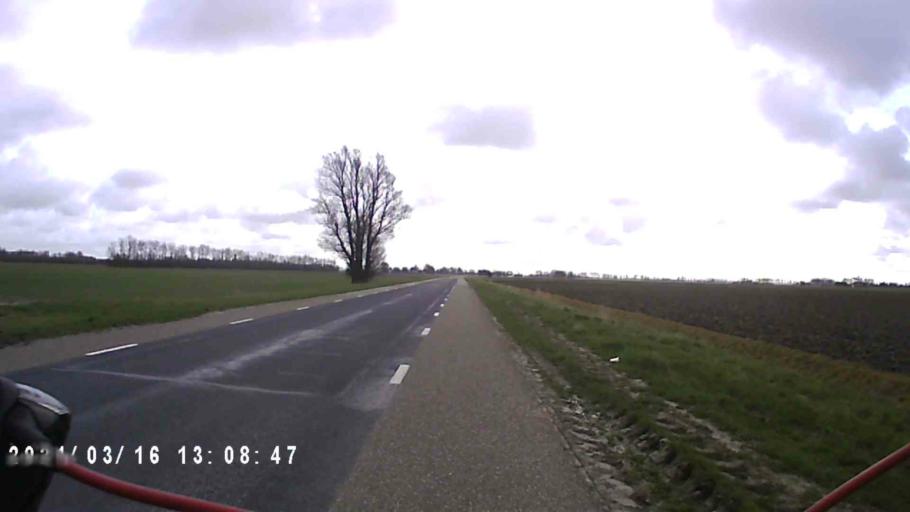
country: NL
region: Friesland
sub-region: Menameradiel
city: Berltsum
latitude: 53.2474
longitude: 5.6236
